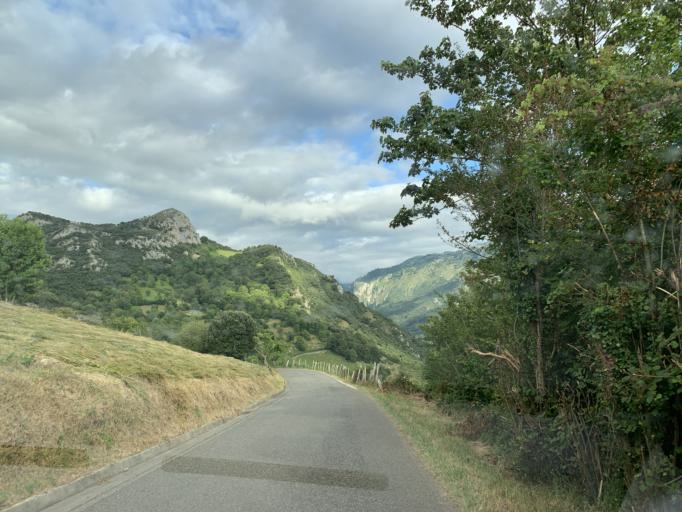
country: ES
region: Asturias
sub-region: Province of Asturias
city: Carrena
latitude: 43.3185
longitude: -4.8506
